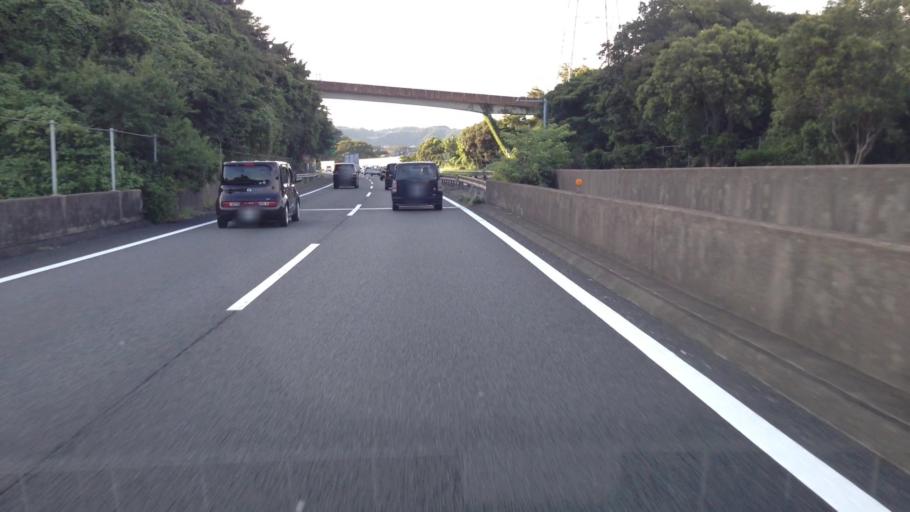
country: JP
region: Kanagawa
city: Zushi
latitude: 35.3171
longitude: 139.6062
